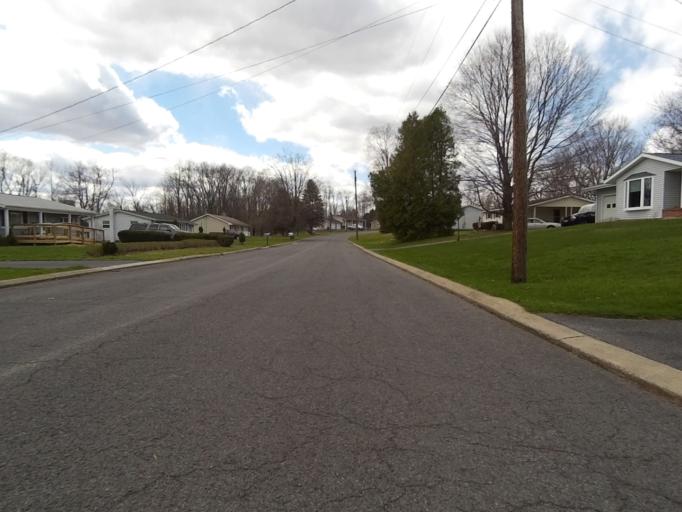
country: US
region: Pennsylvania
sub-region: Centre County
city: Park Forest Village
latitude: 40.8279
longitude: -77.9493
